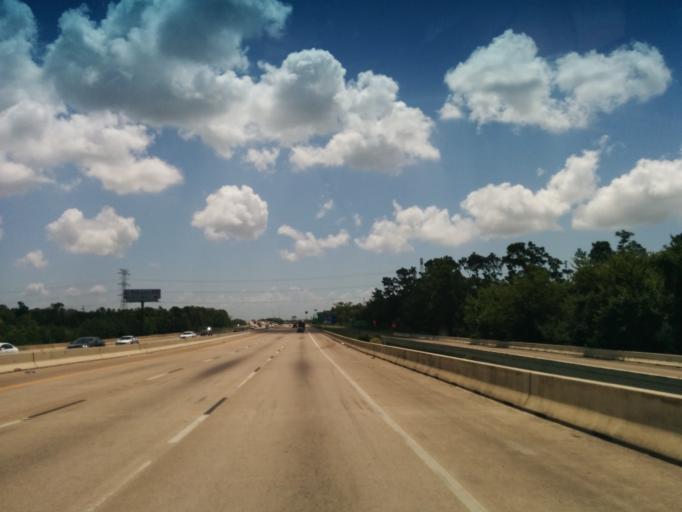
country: US
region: Texas
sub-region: Chambers County
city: Mont Belvieu
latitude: 29.8210
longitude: -94.9108
